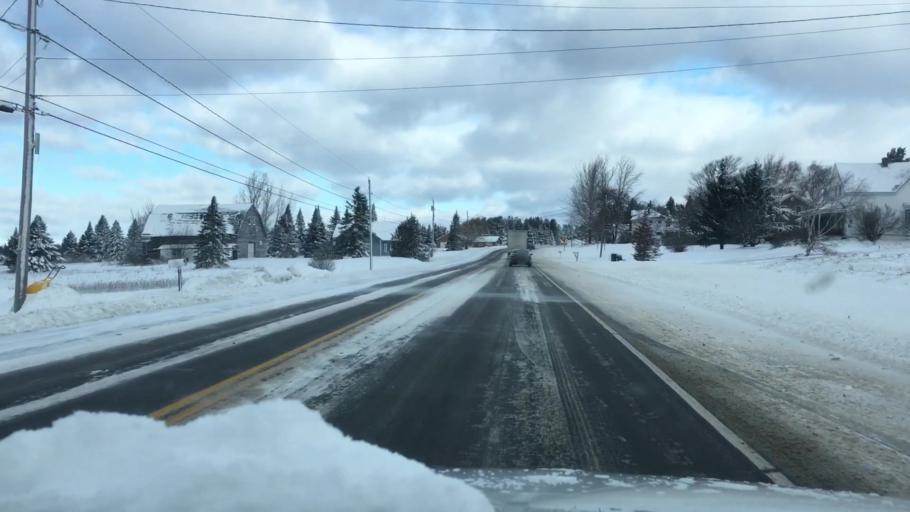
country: US
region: Maine
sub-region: Aroostook County
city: Caribou
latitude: 46.7888
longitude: -67.9902
